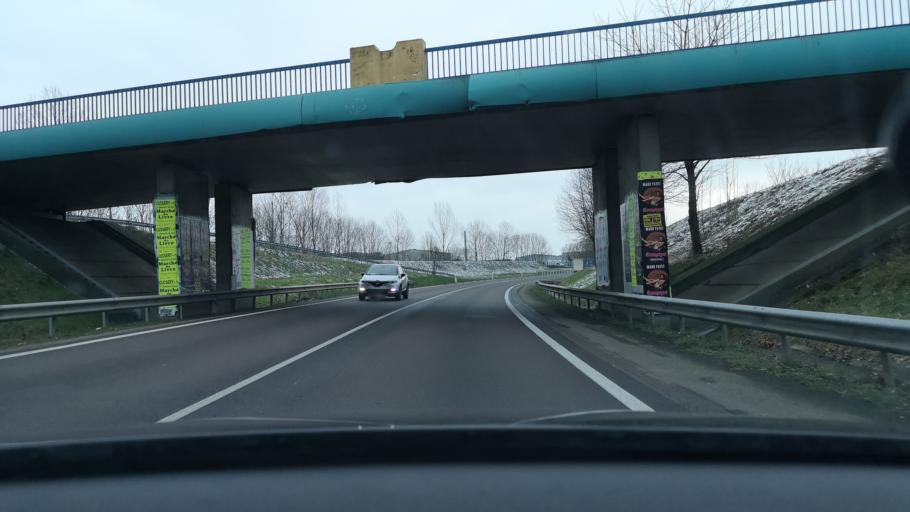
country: FR
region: Bourgogne
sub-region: Departement de Saone-et-Loire
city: Saint-Marcel
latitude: 46.7887
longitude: 4.9043
